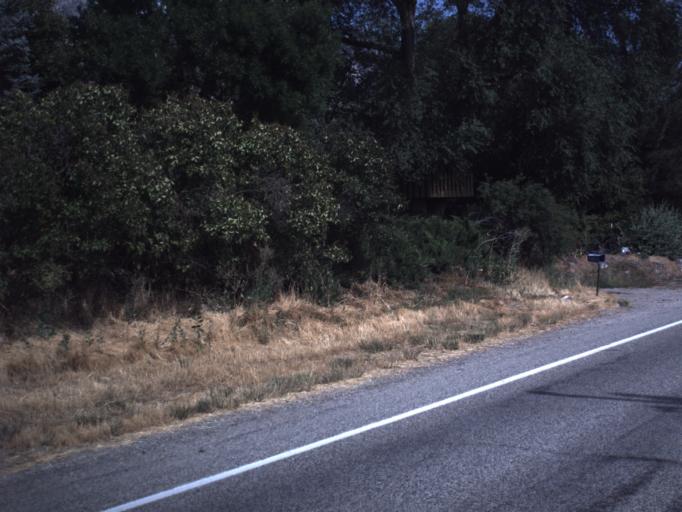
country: US
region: Utah
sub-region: Box Elder County
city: Honeyville
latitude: 41.6080
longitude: -112.0601
